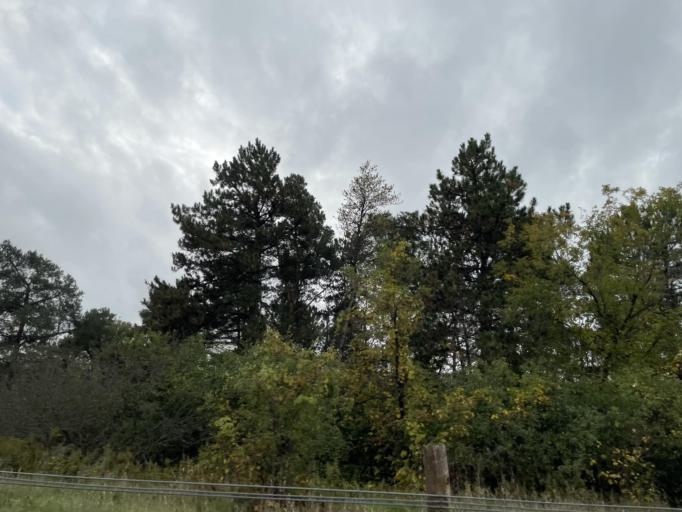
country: CA
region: Ontario
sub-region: Wellington County
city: Guelph
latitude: 43.5593
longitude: -80.2044
